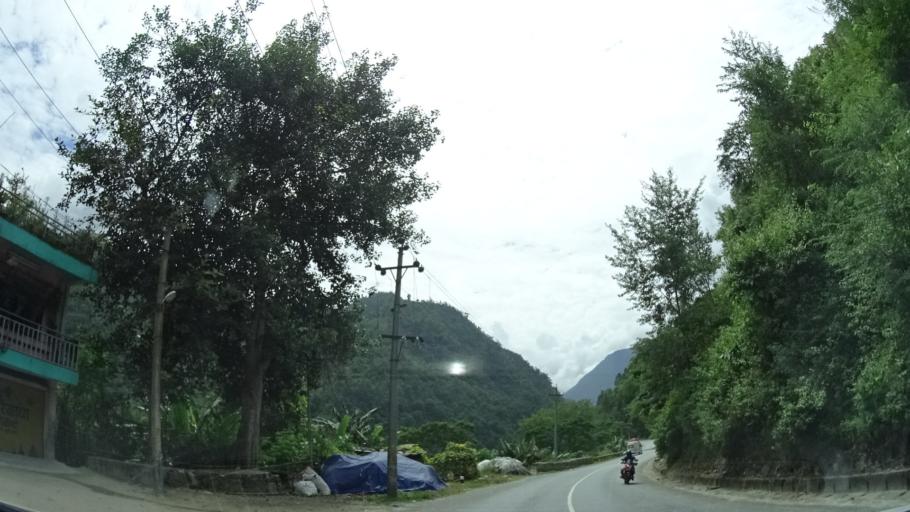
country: NP
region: Central Region
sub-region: Narayani Zone
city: Bharatpur
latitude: 27.8981
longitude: 84.5392
